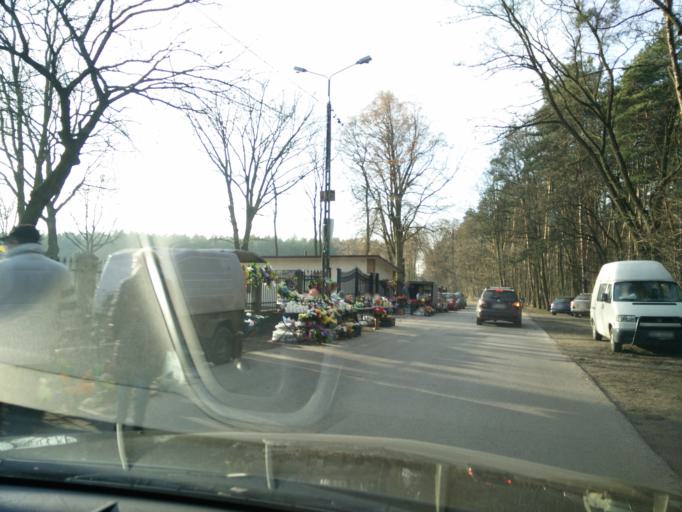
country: PL
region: Masovian Voivodeship
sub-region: Powiat wolominski
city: Nowe Lipiny
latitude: 52.3319
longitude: 21.2718
